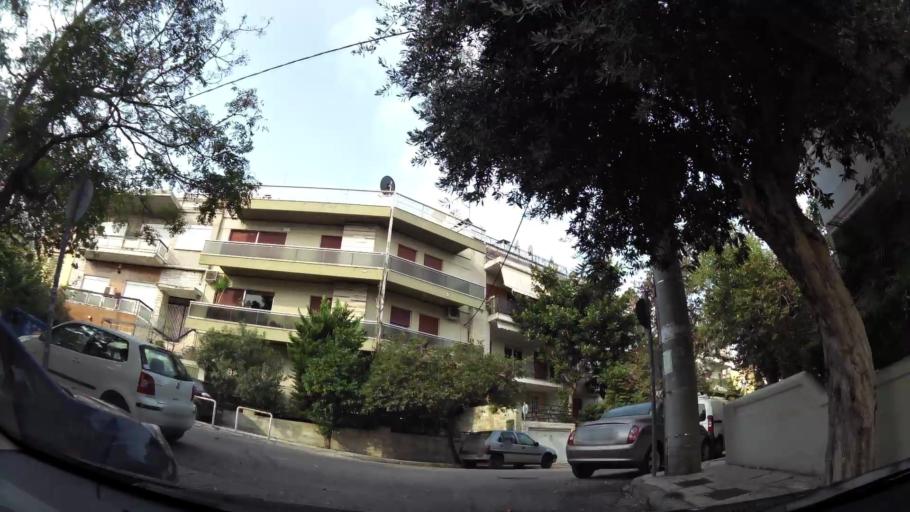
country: GR
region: Attica
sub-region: Nomarchia Athinas
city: Psychiko
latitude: 37.9995
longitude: 23.7615
